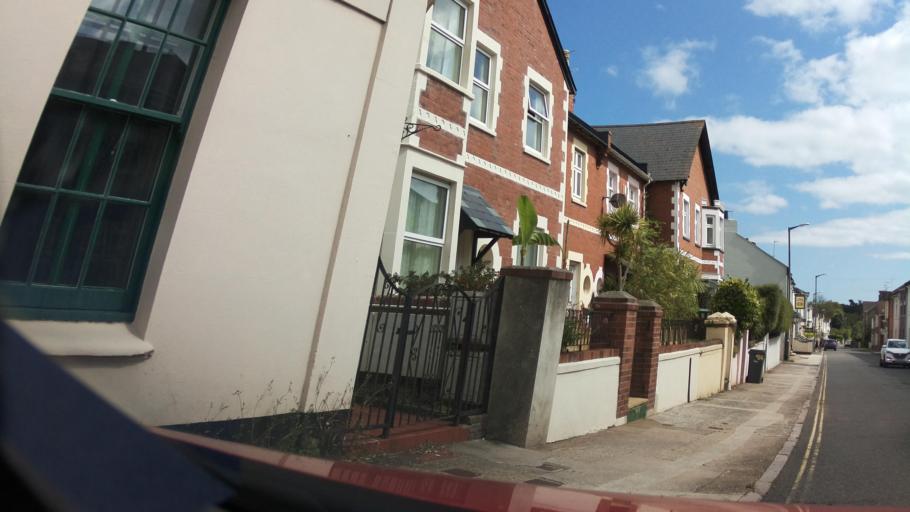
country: GB
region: England
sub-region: Borough of Torbay
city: Torquay
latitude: 50.4773
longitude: -3.5128
